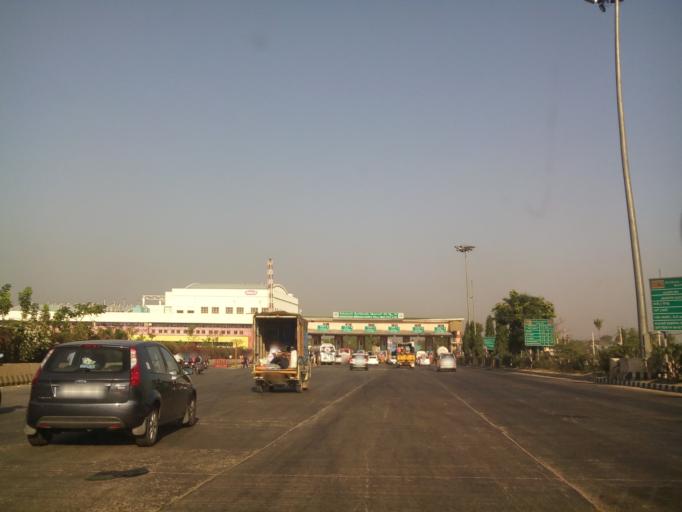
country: IN
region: Karnataka
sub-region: Bangalore Rural
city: Nelamangala
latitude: 13.0492
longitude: 77.4957
